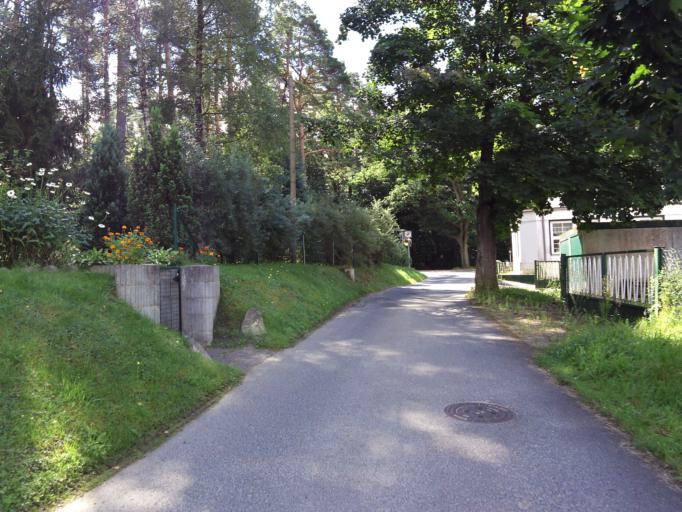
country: DE
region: Brandenburg
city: Lychen
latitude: 53.2156
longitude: 13.2799
